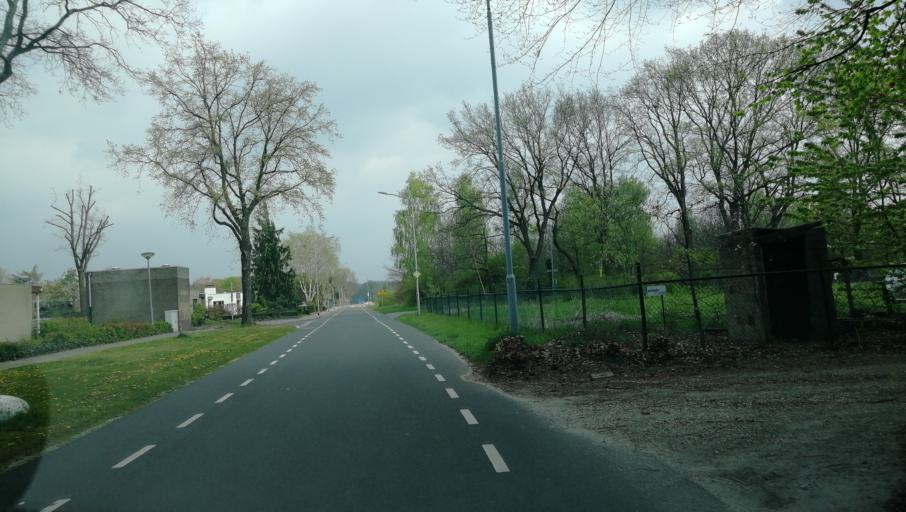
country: NL
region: Limburg
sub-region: Gemeente Venlo
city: Venlo
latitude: 51.3603
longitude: 6.1967
